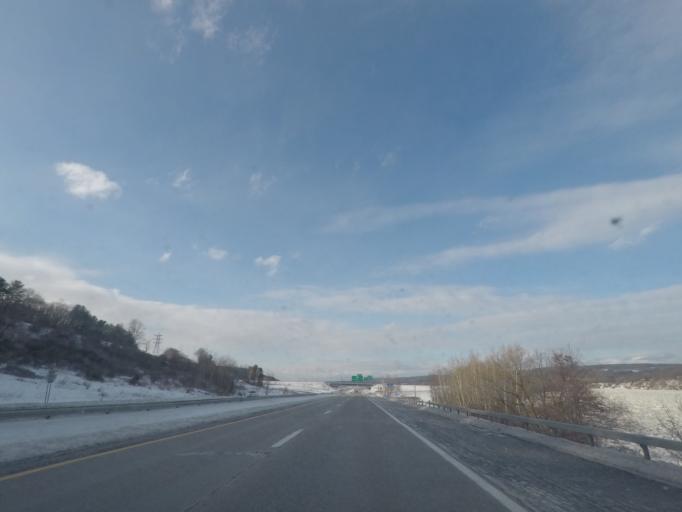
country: US
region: New York
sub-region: Schenectady County
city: Scotia
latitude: 42.8372
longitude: -73.9997
